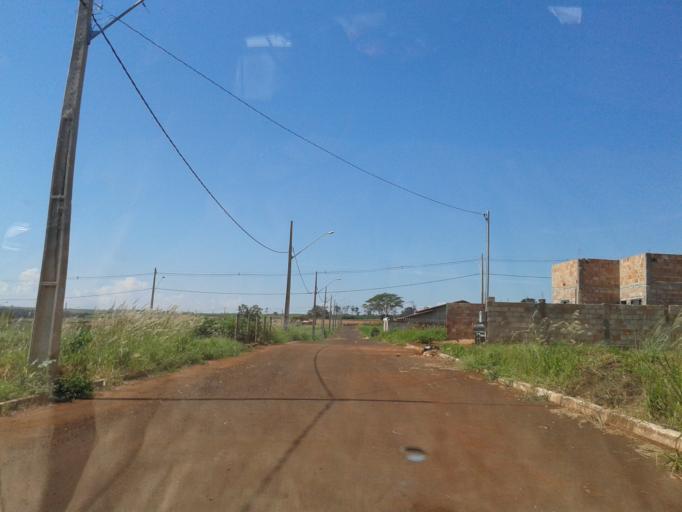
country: BR
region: Goias
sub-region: Itumbiara
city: Itumbiara
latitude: -18.4252
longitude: -49.1846
